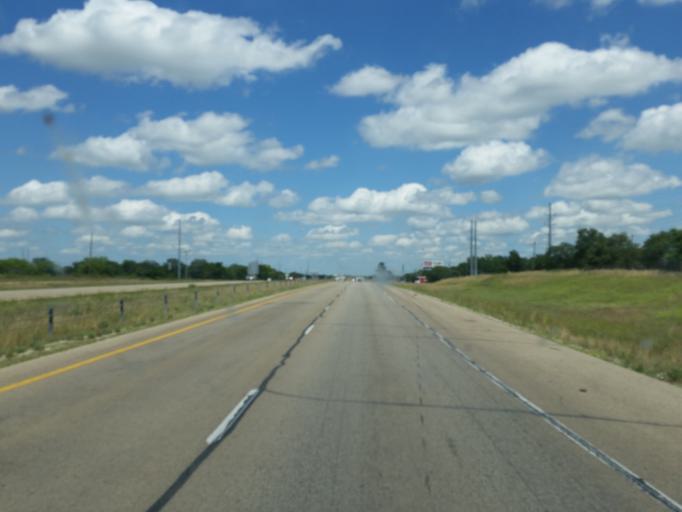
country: US
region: Texas
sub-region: Callahan County
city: Clyde
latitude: 32.4171
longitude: -99.5196
